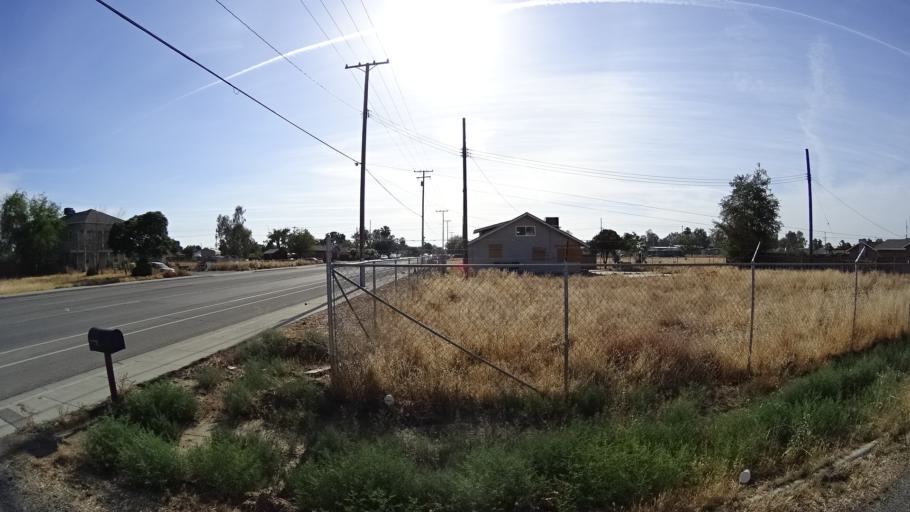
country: US
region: California
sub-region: Kings County
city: Hanford
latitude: 36.3133
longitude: -119.6482
